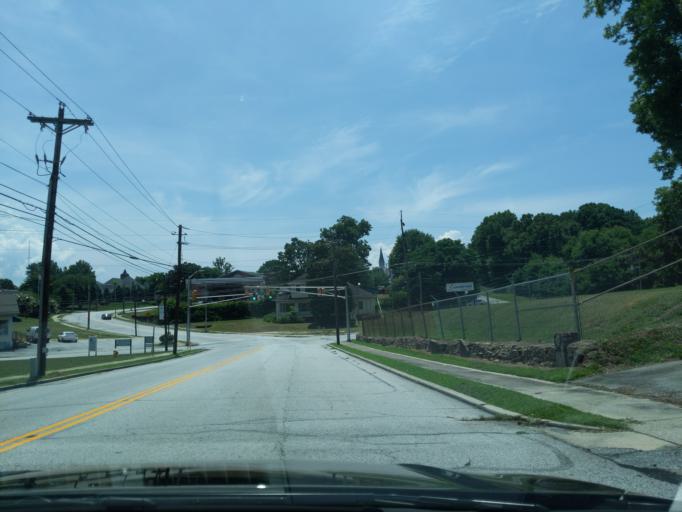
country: US
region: South Carolina
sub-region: Laurens County
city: Laurens
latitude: 34.5017
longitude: -82.0203
